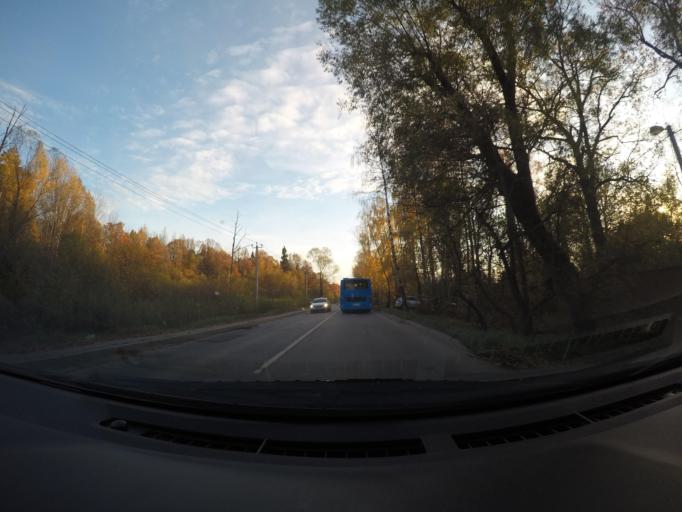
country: RU
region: Moskovskaya
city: Firsanovka
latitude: 55.9467
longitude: 37.2509
